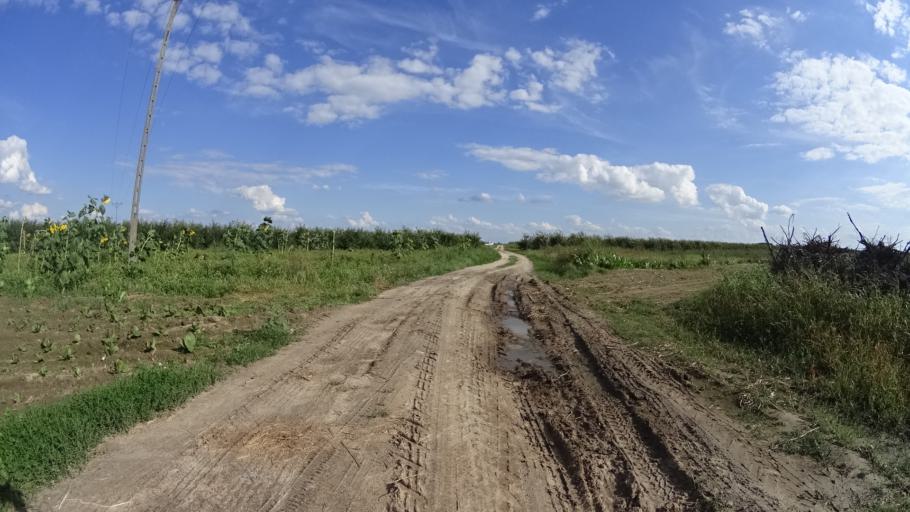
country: PL
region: Masovian Voivodeship
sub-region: Powiat bialobrzeski
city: Wysmierzyce
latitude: 51.6633
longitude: 20.8162
